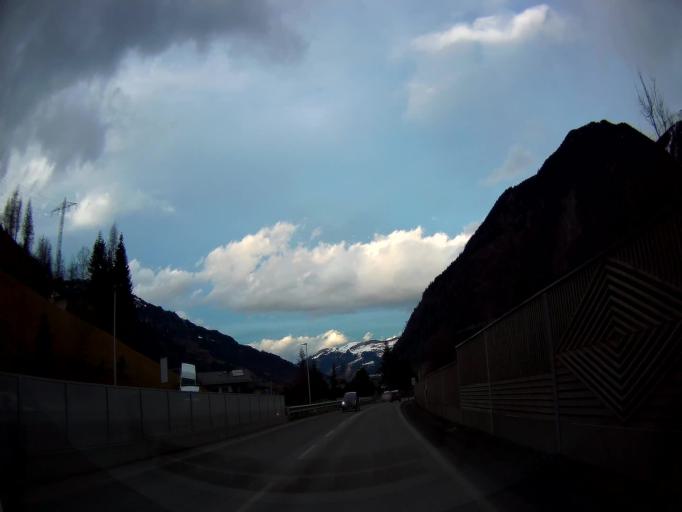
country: AT
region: Salzburg
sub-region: Politischer Bezirk Sankt Johann im Pongau
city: Bad Hofgastein
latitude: 47.1717
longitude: 13.0979
